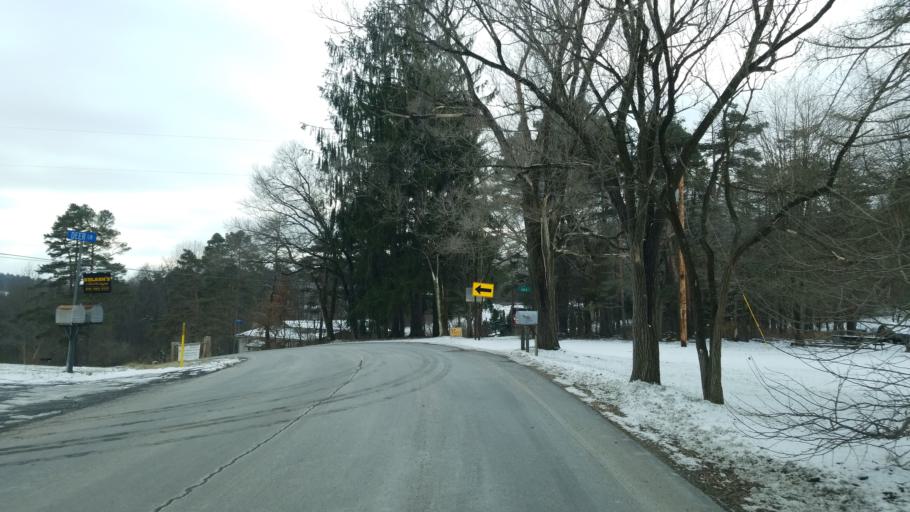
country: US
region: Pennsylvania
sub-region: Clearfield County
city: Sandy
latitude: 41.0873
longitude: -78.7500
